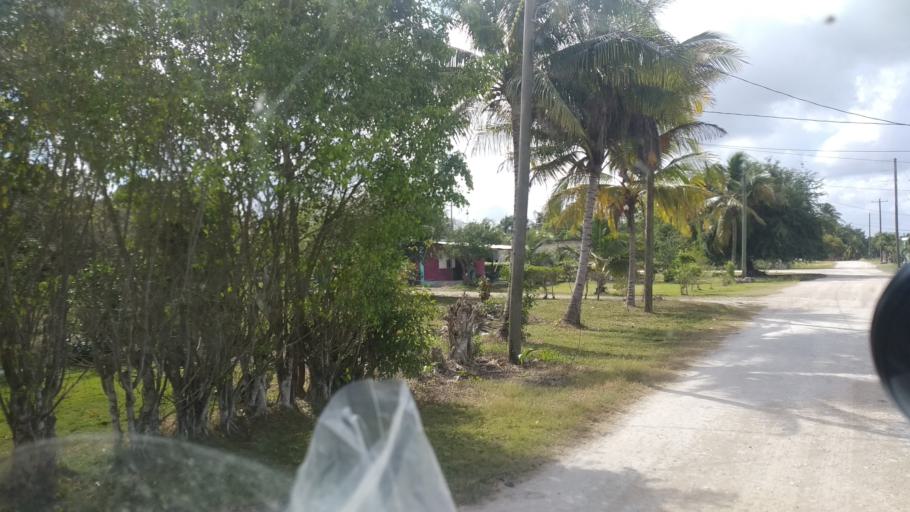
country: BZ
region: Corozal
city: Corozal
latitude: 18.3504
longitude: -88.4991
